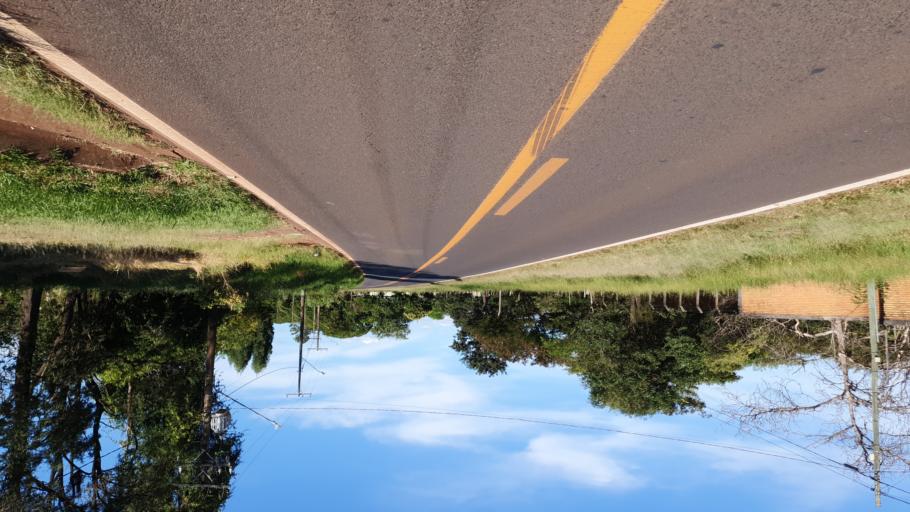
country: BR
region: Sao Paulo
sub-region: Paraguacu Paulista
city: Paraguacu Paulista
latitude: -22.4023
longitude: -50.5715
